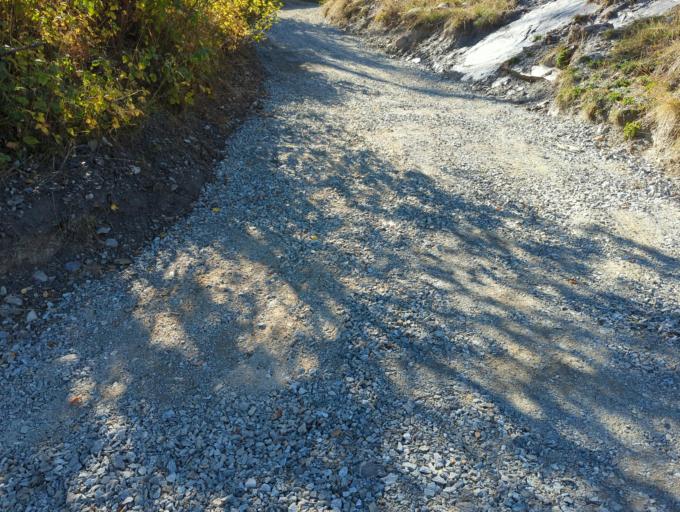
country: FR
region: Rhone-Alpes
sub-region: Departement de la Savoie
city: Saint-Jean-de-Maurienne
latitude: 45.2583
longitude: 6.2722
